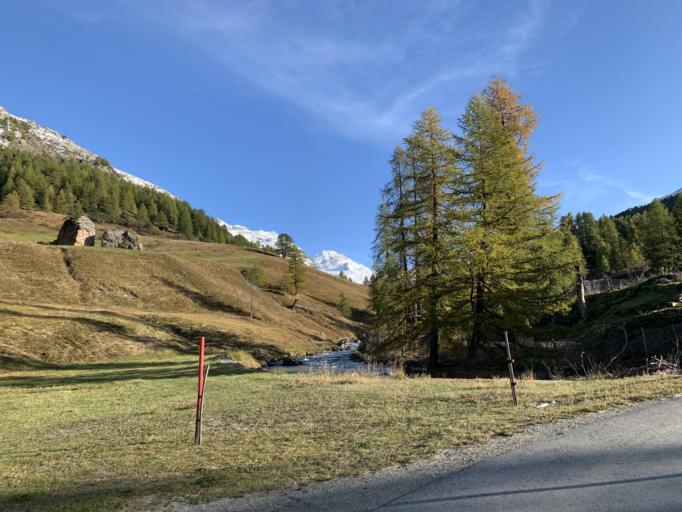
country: CH
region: Grisons
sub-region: Maloja District
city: Silvaplana
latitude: 46.4179
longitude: 9.7647
